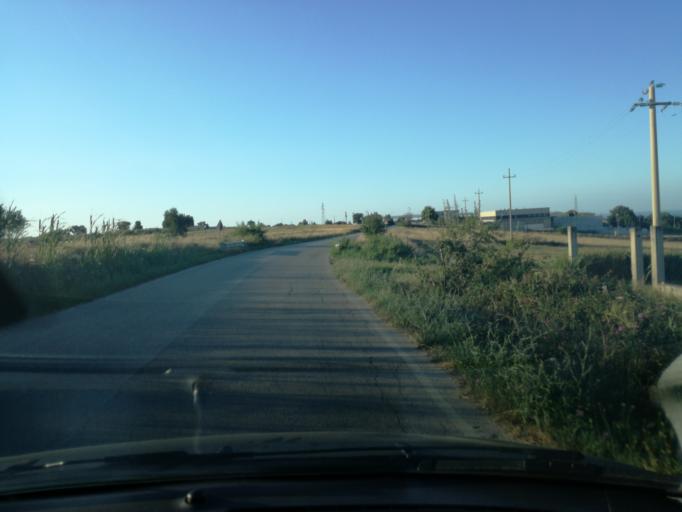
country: IT
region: Molise
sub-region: Provincia di Campobasso
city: San Giacomo degli Schiavoni
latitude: 41.9540
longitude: 14.9434
